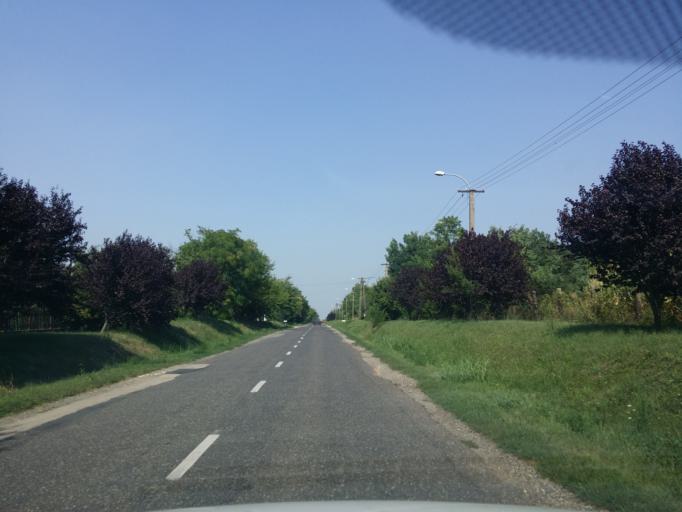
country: HU
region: Fejer
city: Sarbogard
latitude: 46.9285
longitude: 18.6838
